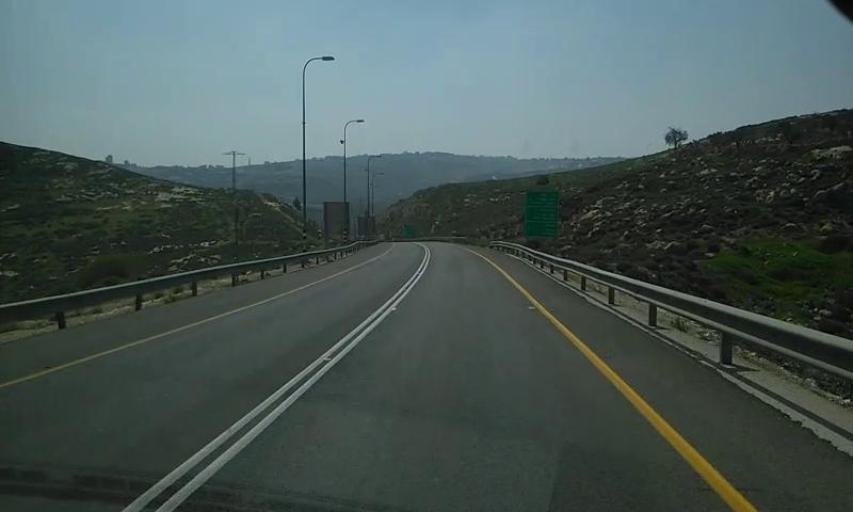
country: PS
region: West Bank
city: Mikhmas
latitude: 31.8771
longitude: 35.2661
